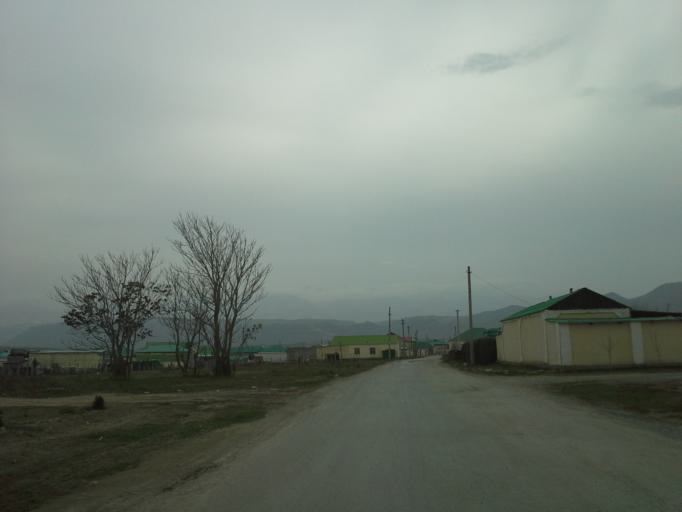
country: TM
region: Ahal
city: Abadan
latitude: 37.9819
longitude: 58.2255
